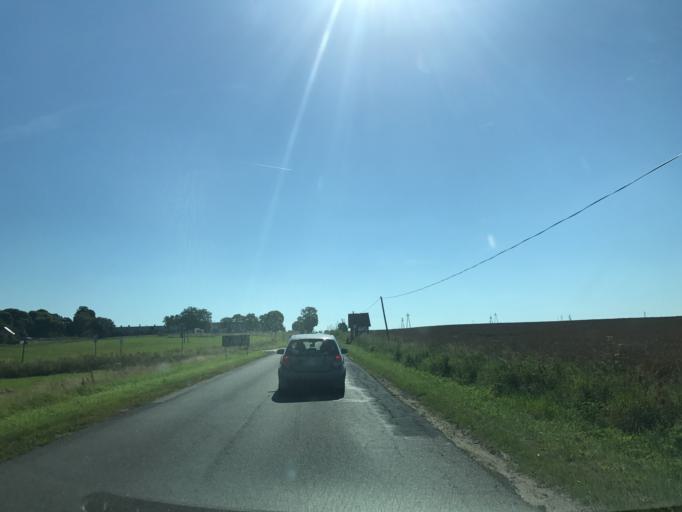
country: PL
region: Pomeranian Voivodeship
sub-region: Powiat bytowski
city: Czarna Dabrowka
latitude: 54.3665
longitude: 17.5050
